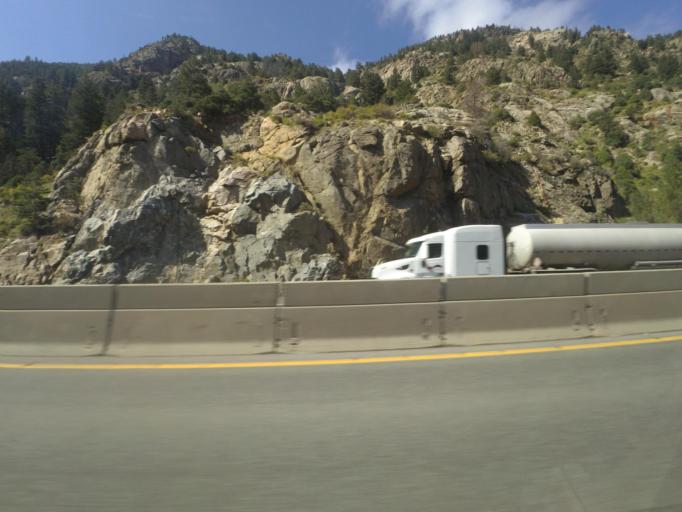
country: US
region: Colorado
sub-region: Clear Creek County
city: Georgetown
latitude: 39.7057
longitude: -105.7042
